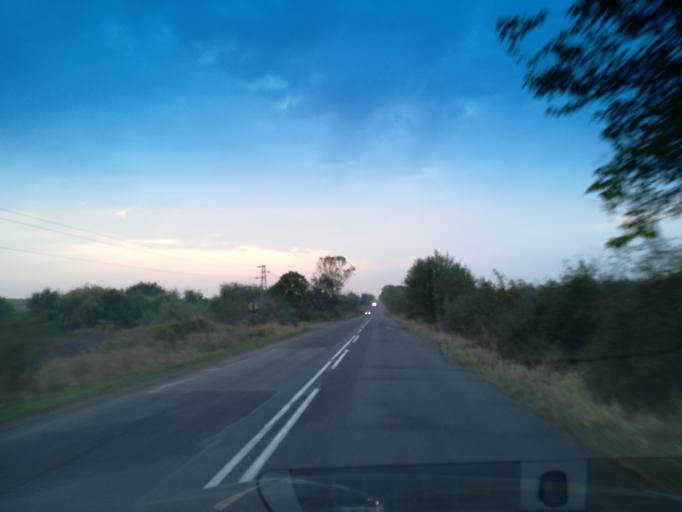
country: BG
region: Stara Zagora
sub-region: Obshtina Chirpan
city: Chirpan
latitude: 42.1851
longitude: 25.2630
